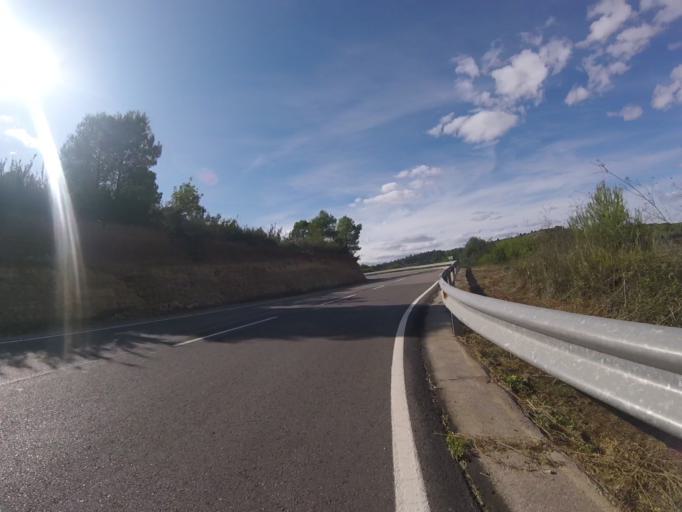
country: ES
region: Valencia
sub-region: Provincia de Castello
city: Cuevas de Vinroma
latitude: 40.2968
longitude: 0.1677
